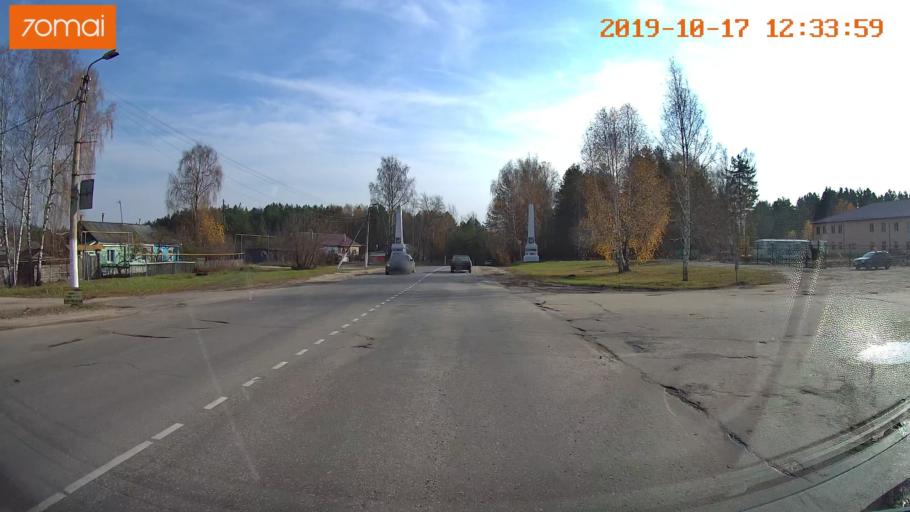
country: RU
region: Rjazan
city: Kasimov
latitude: 54.9507
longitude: 41.3602
